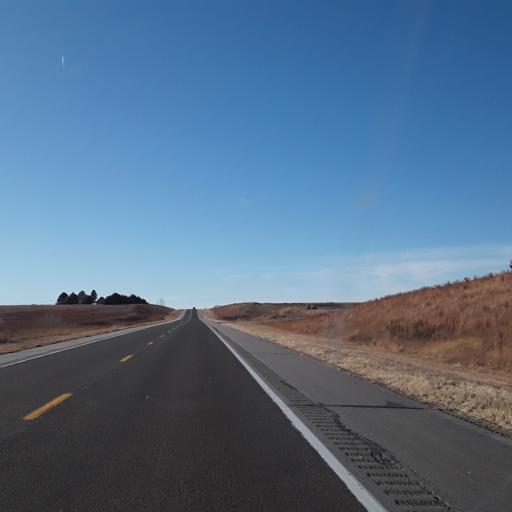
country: US
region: Nebraska
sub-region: Hitchcock County
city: Trenton
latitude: 40.1764
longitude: -101.0794
